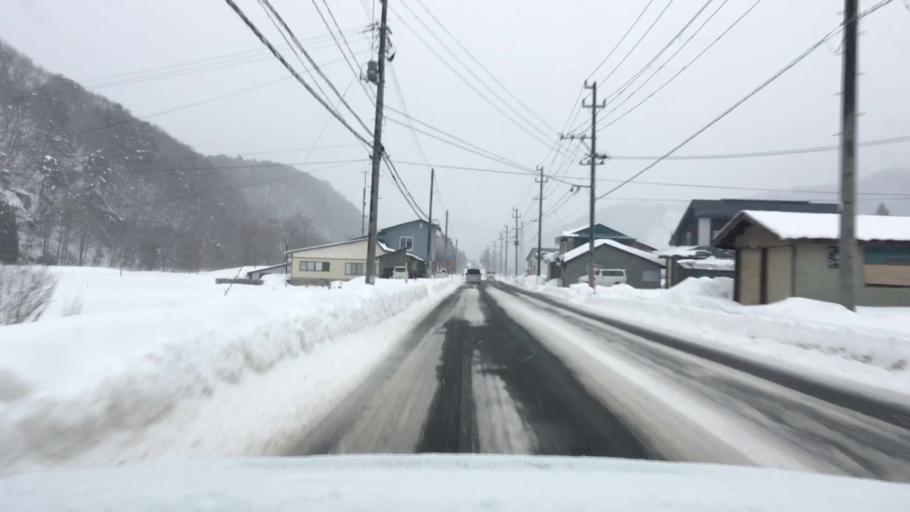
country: JP
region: Akita
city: Hanawa
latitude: 40.0569
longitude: 141.0101
